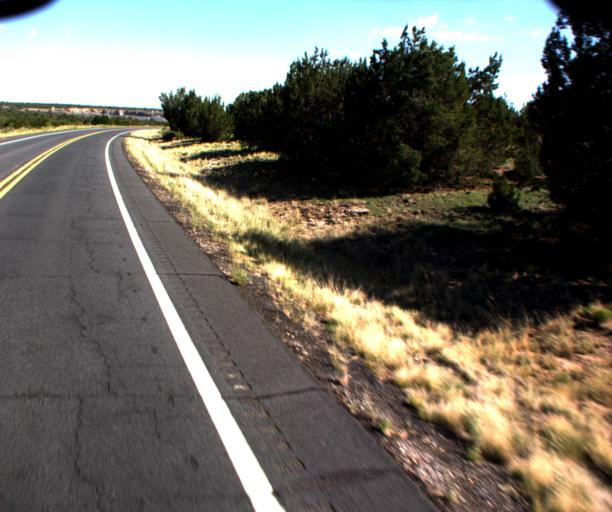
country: US
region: Arizona
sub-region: Coconino County
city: Williams
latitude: 35.4745
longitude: -112.1769
